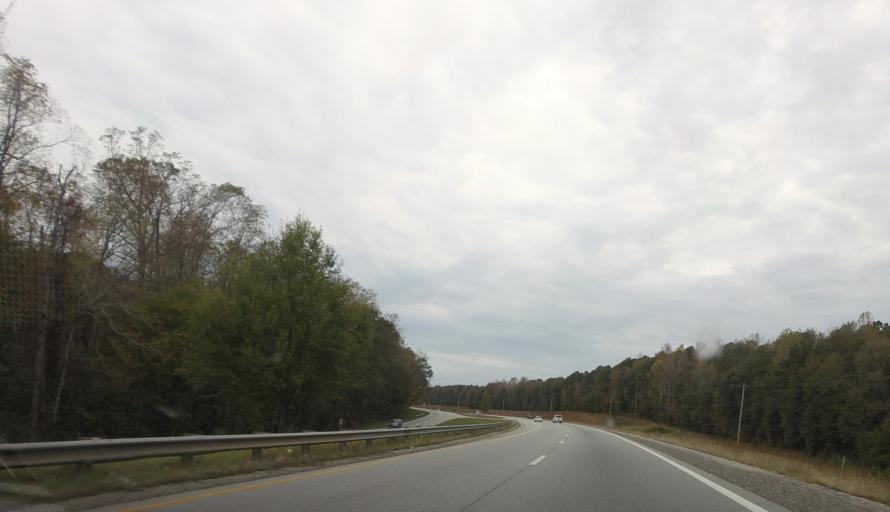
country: US
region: Alabama
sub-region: Lee County
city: Opelika
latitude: 32.6338
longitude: -85.2866
